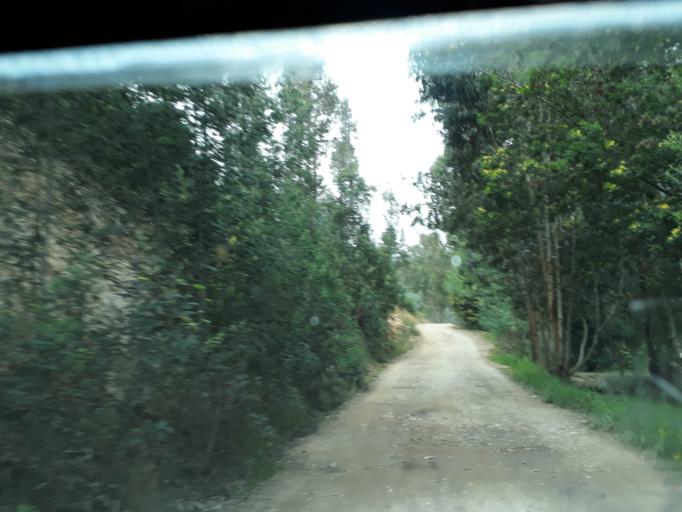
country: CO
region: Cundinamarca
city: Cucunuba
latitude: 5.2630
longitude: -73.7719
